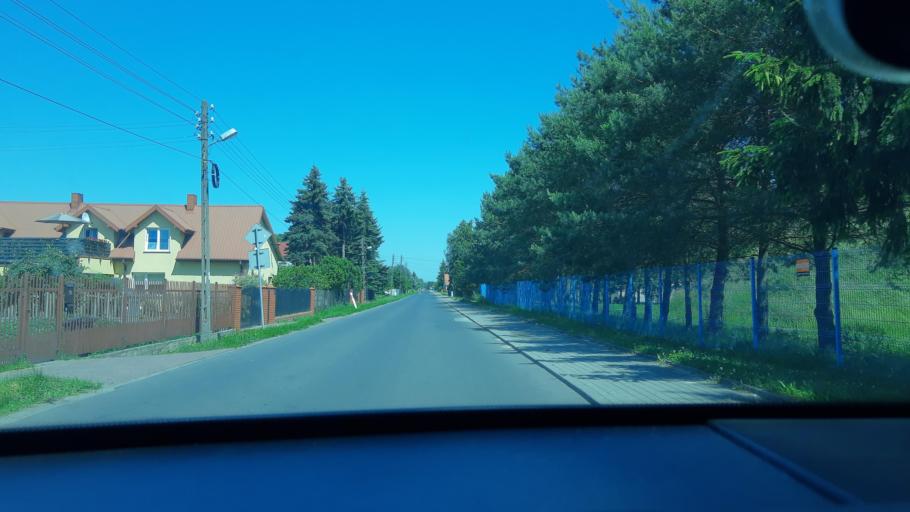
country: PL
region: Lodz Voivodeship
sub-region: Powiat zdunskowolski
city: Zdunska Wola
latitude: 51.6200
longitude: 18.9369
